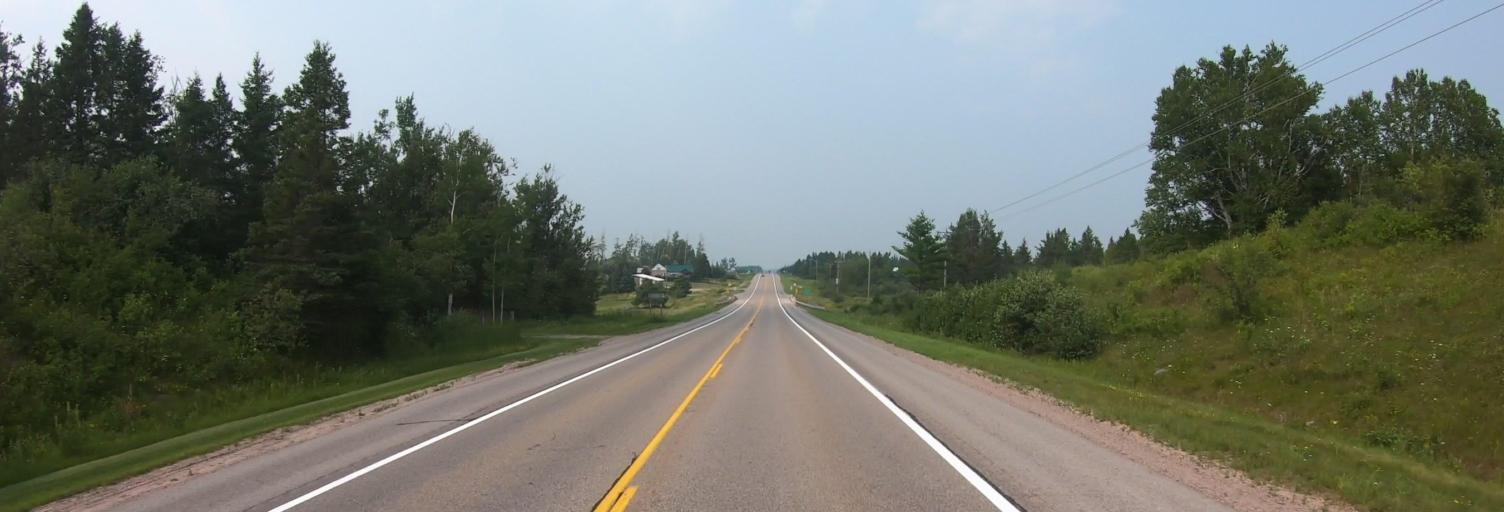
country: US
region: Michigan
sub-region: Chippewa County
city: Sault Ste. Marie
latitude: 46.3328
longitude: -84.3640
